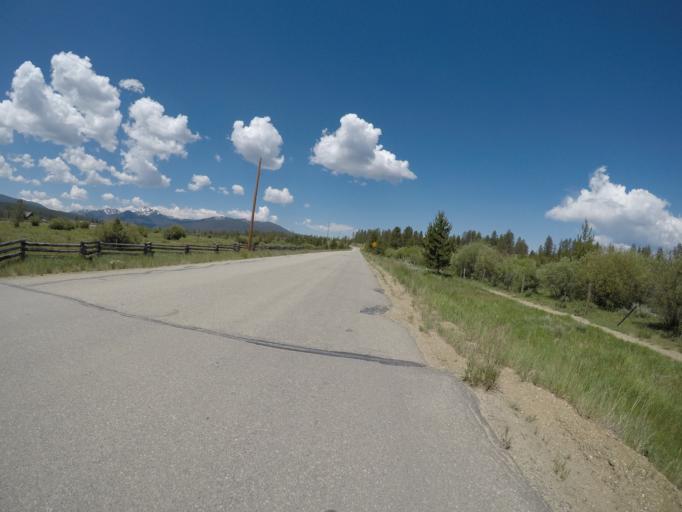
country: US
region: Colorado
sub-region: Grand County
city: Fraser
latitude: 39.9447
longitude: -105.8269
